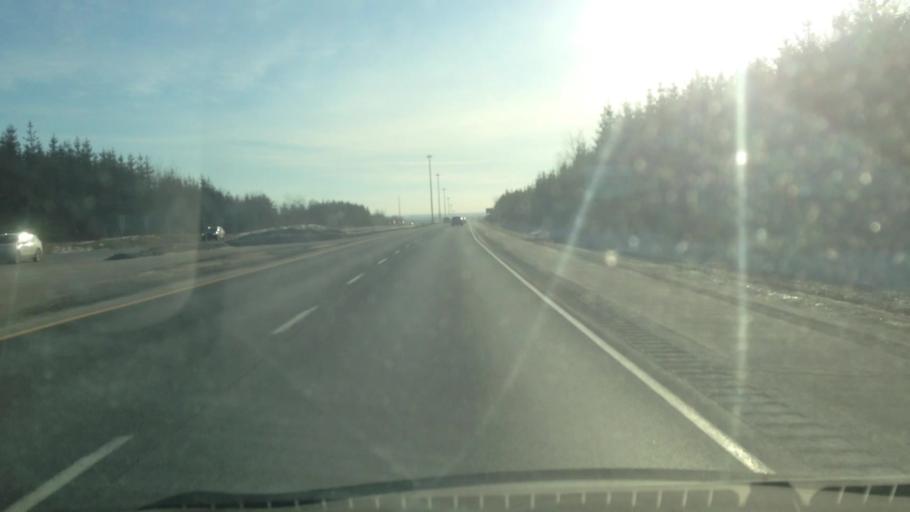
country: CA
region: Quebec
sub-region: Laurentides
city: Saint-Jerome
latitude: 45.8072
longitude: -74.0391
